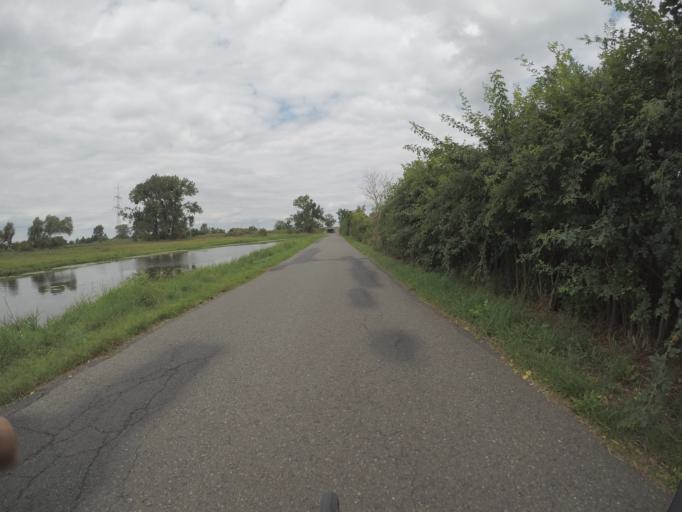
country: DE
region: Brandenburg
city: Wustermark
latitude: 52.5975
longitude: 12.9347
